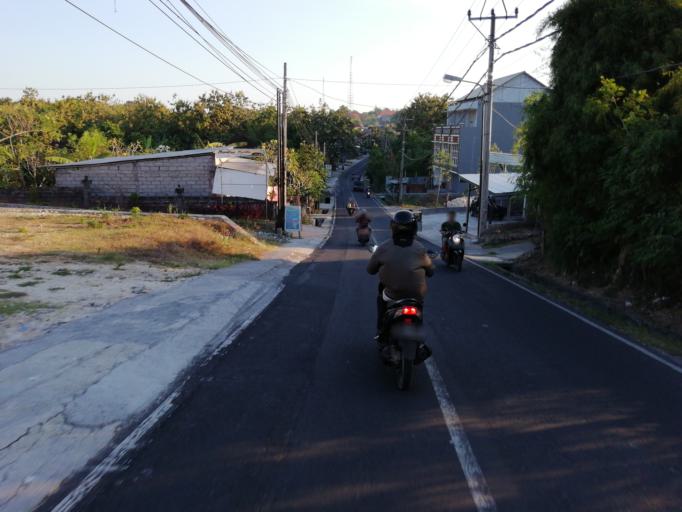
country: ID
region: Bali
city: Bualu
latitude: -8.8209
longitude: 115.1885
